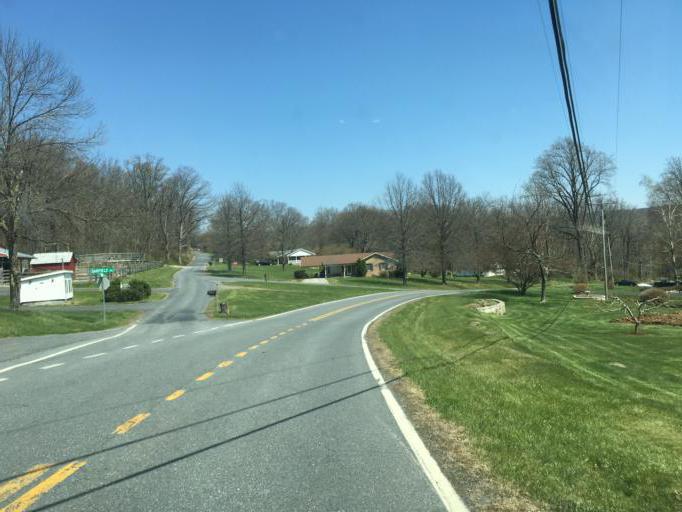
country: US
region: Maryland
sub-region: Washington County
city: Smithsburg
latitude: 39.6143
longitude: -77.5396
